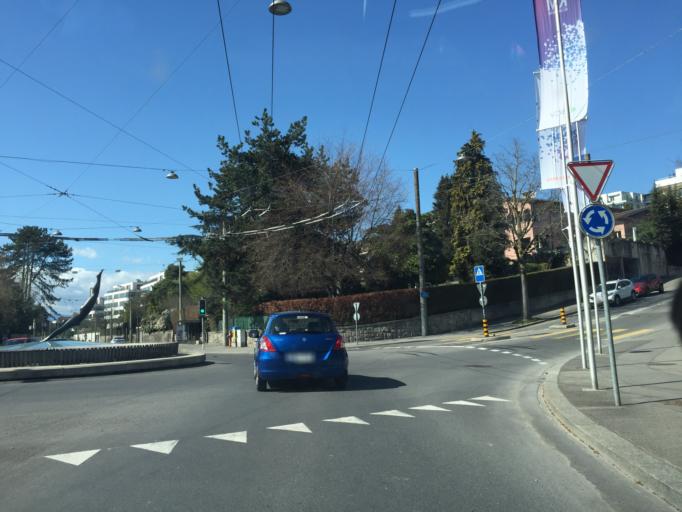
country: CH
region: Vaud
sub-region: Lausanne District
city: Lausanne
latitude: 46.5116
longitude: 6.6174
